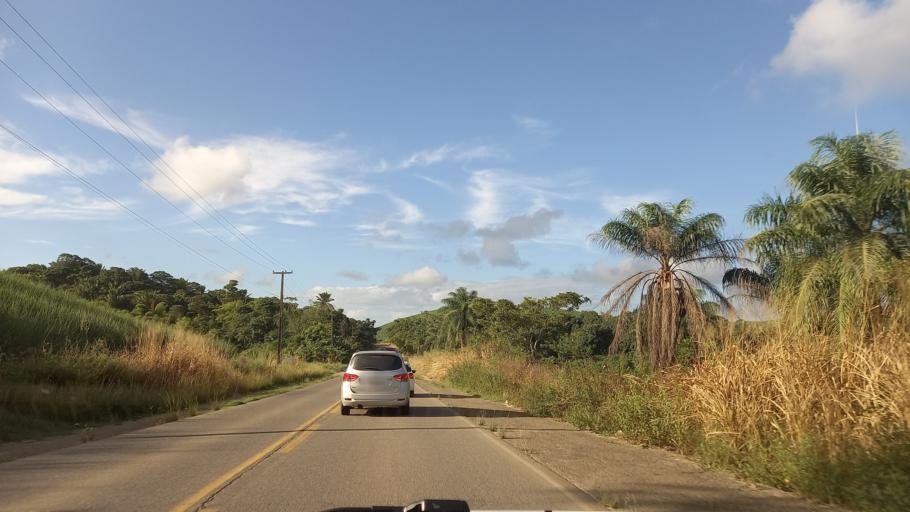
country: BR
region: Pernambuco
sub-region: Sirinhaem
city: Sirinhaem
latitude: -8.6170
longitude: -35.1210
